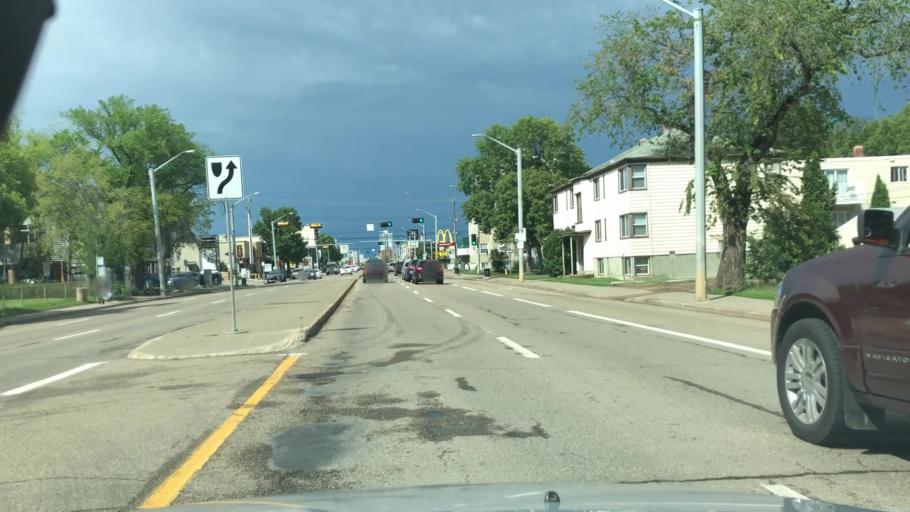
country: CA
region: Alberta
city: Edmonton
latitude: 53.5193
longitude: -113.5120
